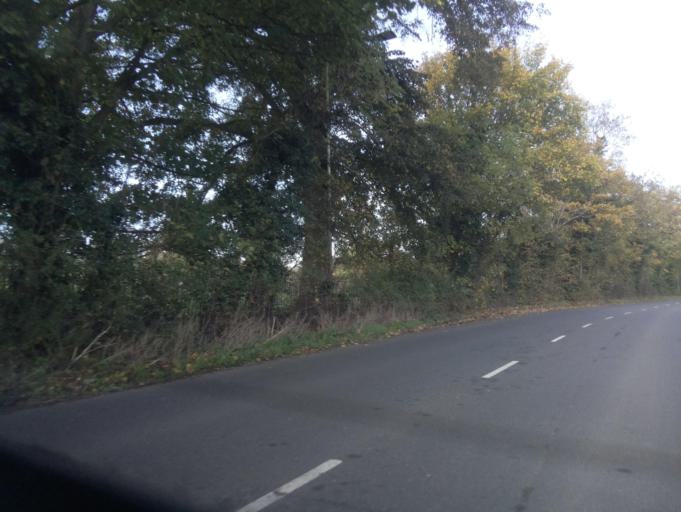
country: GB
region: England
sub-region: Wiltshire
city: Bradford-on-Avon
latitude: 51.3557
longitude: -2.2537
